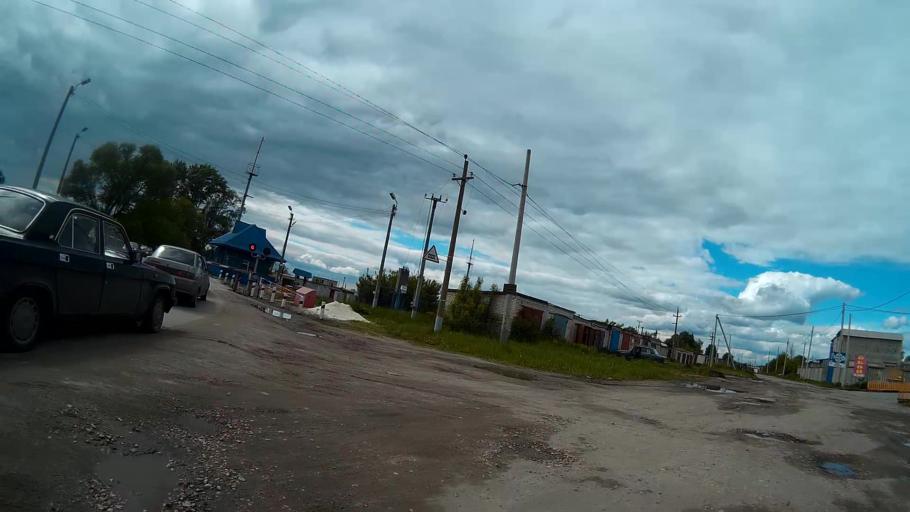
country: RU
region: Ulyanovsk
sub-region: Ulyanovskiy Rayon
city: Ulyanovsk
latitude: 54.2572
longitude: 48.3128
